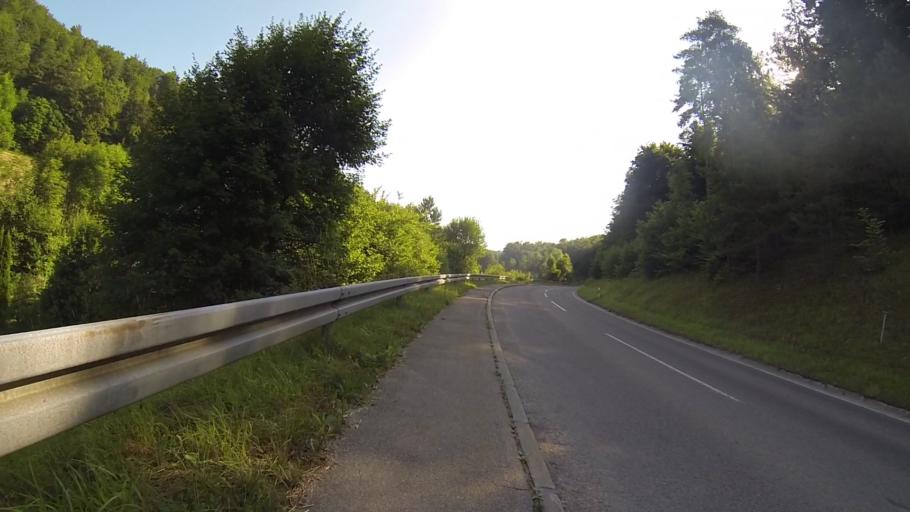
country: DE
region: Baden-Wuerttemberg
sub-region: Regierungsbezirk Stuttgart
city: Konigsbronn
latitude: 48.7370
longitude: 10.1388
